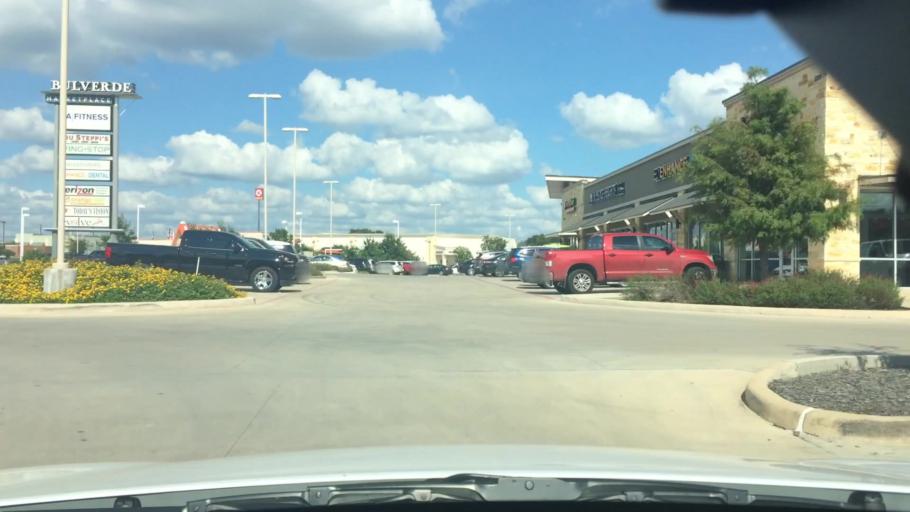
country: US
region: Texas
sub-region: Bexar County
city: Hollywood Park
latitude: 29.5980
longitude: -98.4207
